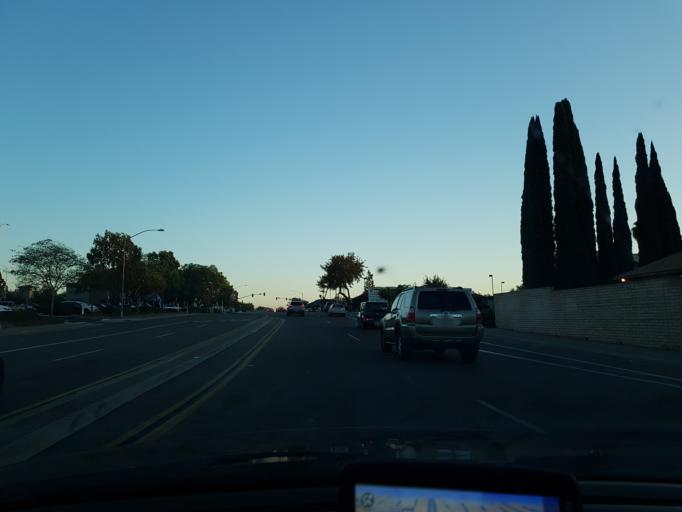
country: US
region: California
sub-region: San Diego County
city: Fairbanks Ranch
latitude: 32.9193
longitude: -117.1251
